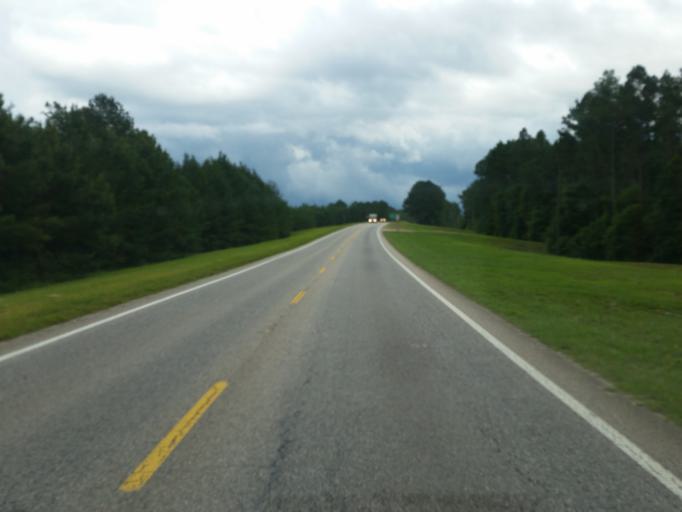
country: US
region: Mississippi
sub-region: George County
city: Lucedale
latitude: 30.8601
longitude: -88.4132
